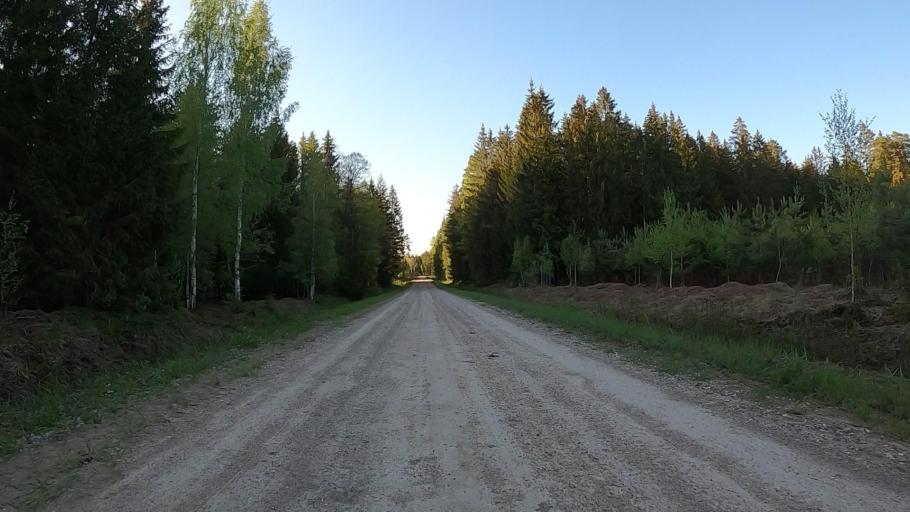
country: LV
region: Kekava
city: Kekava
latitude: 56.7520
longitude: 24.2310
